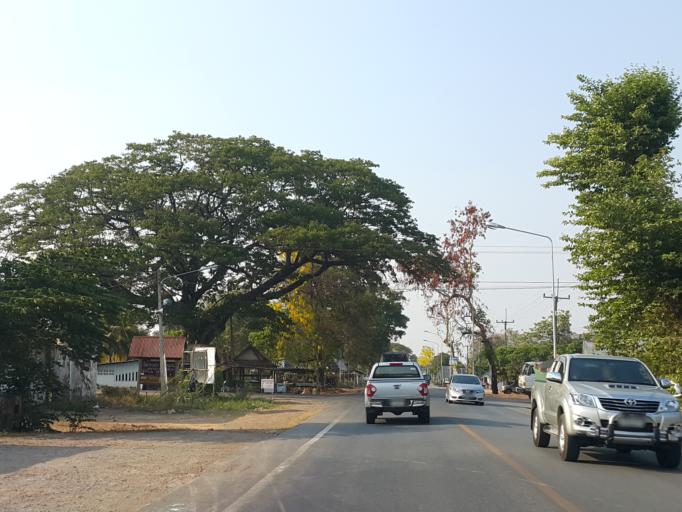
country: TH
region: Phitsanulok
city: Phrom Phiram
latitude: 16.9811
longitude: 100.2119
